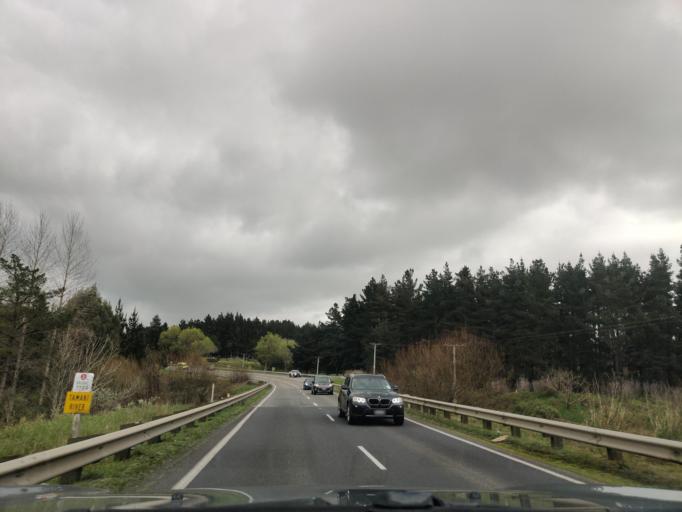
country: NZ
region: Manawatu-Wanganui
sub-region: Palmerston North City
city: Palmerston North
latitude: -40.2292
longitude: 176.0692
